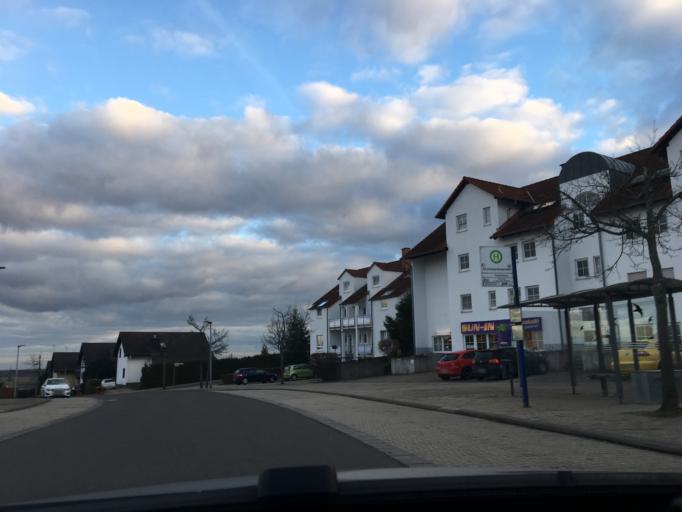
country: DE
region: Rheinland-Pfalz
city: Kirchheimbolanden
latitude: 49.6703
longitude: 7.9972
